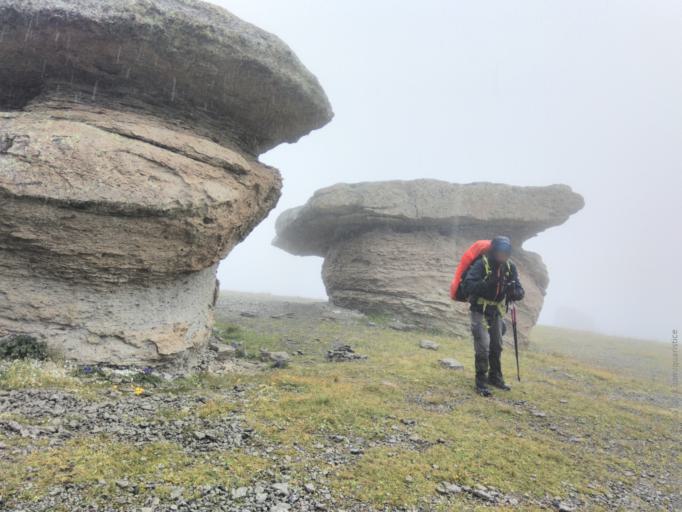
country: RU
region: Kabardino-Balkariya
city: Terskol
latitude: 43.4037
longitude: 42.5003
